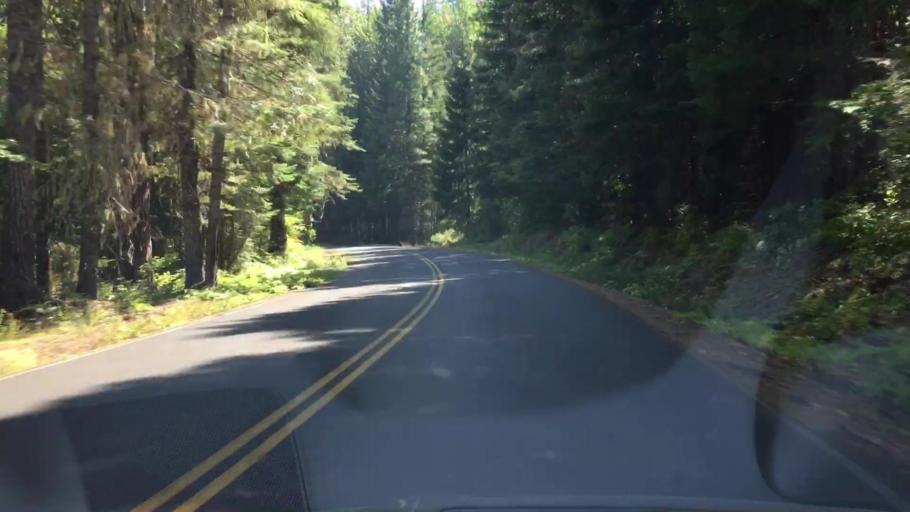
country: US
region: Washington
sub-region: Klickitat County
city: White Salmon
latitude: 46.0569
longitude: -121.5675
